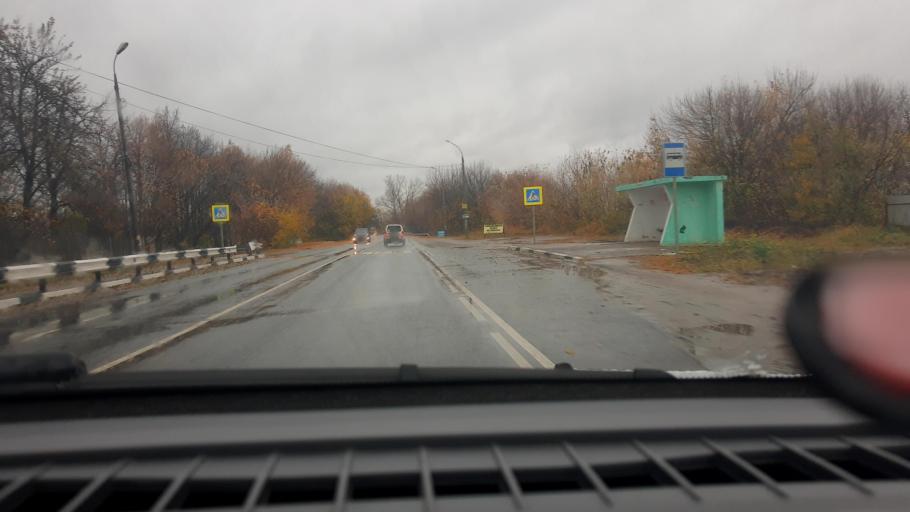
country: RU
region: Nizjnij Novgorod
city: Kstovo
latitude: 56.1390
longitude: 44.1839
